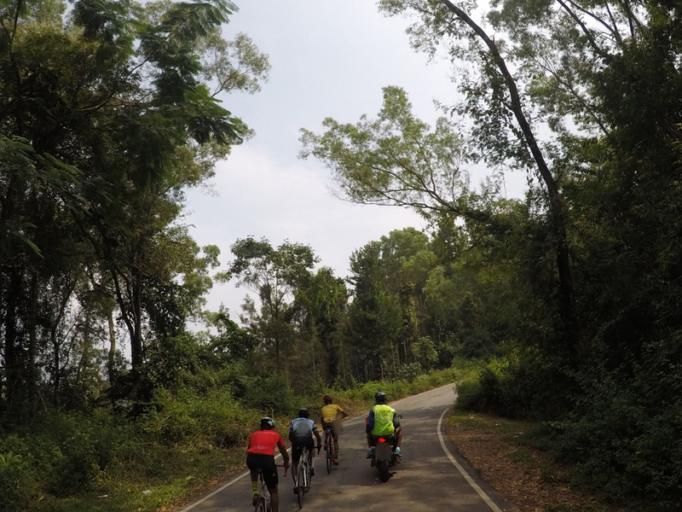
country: IN
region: Karnataka
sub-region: Chikmagalur
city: Mudigere
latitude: 13.1968
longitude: 75.4010
